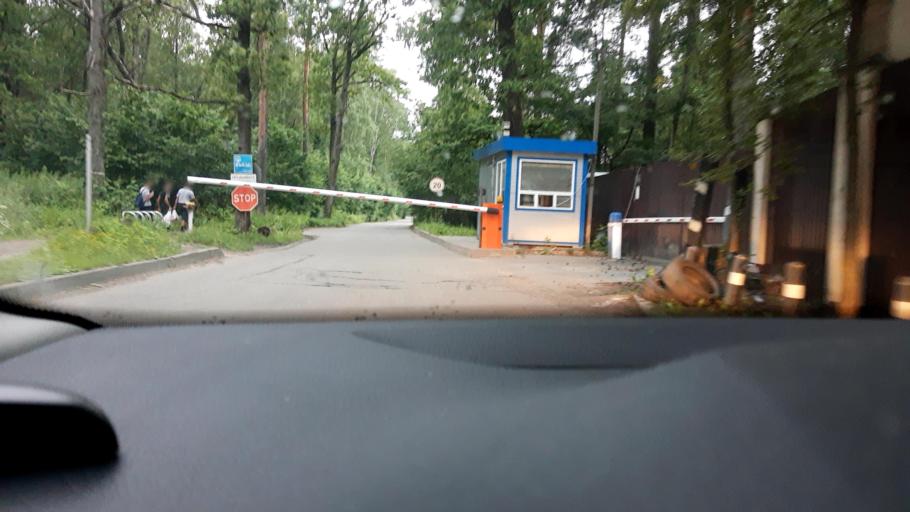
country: RU
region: Moskovskaya
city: Novopodrezkovo
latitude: 55.8922
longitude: 37.3410
